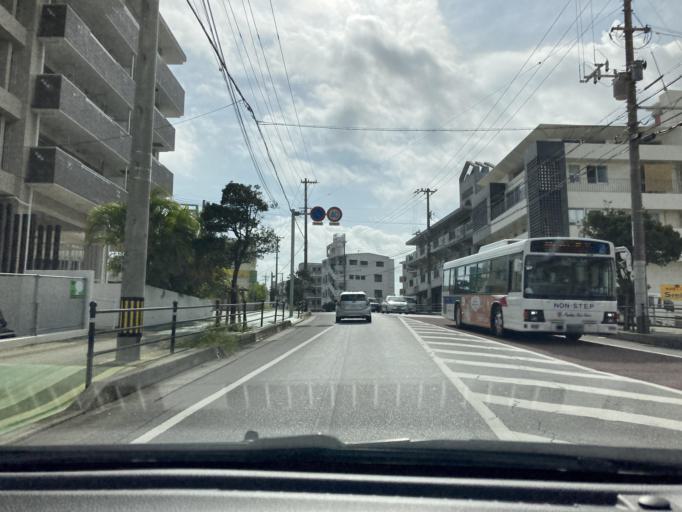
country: JP
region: Okinawa
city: Ginowan
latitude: 26.2620
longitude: 127.7510
